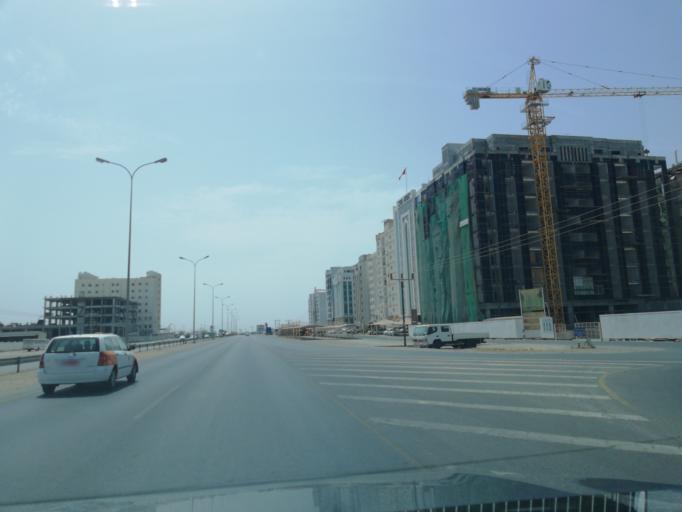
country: OM
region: Muhafazat Masqat
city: Bawshar
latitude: 23.5828
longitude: 58.3708
